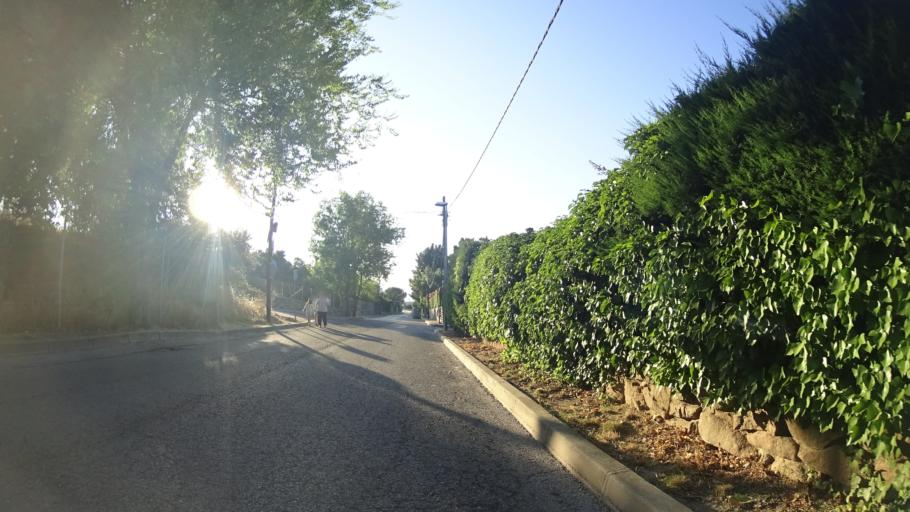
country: ES
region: Madrid
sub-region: Provincia de Madrid
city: Galapagar
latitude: 40.5684
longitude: -4.0045
